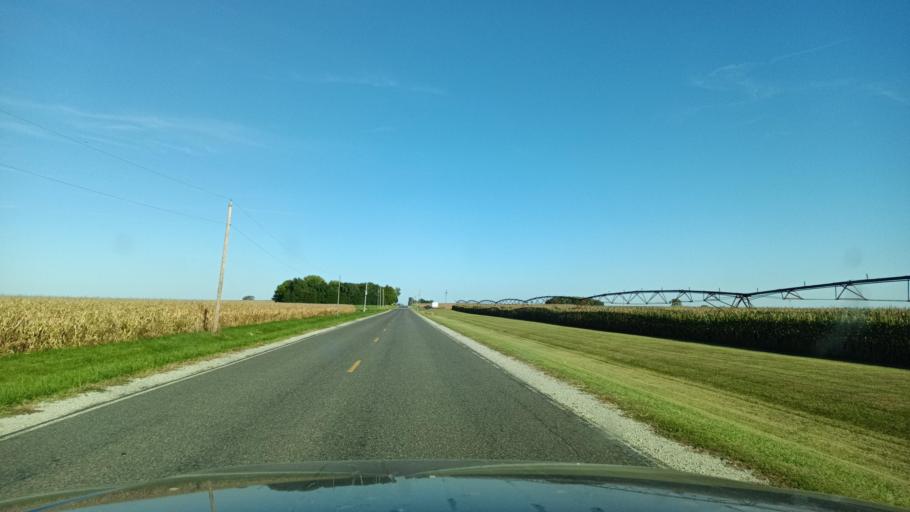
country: US
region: Illinois
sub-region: De Witt County
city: Clinton
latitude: 40.2245
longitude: -88.9215
